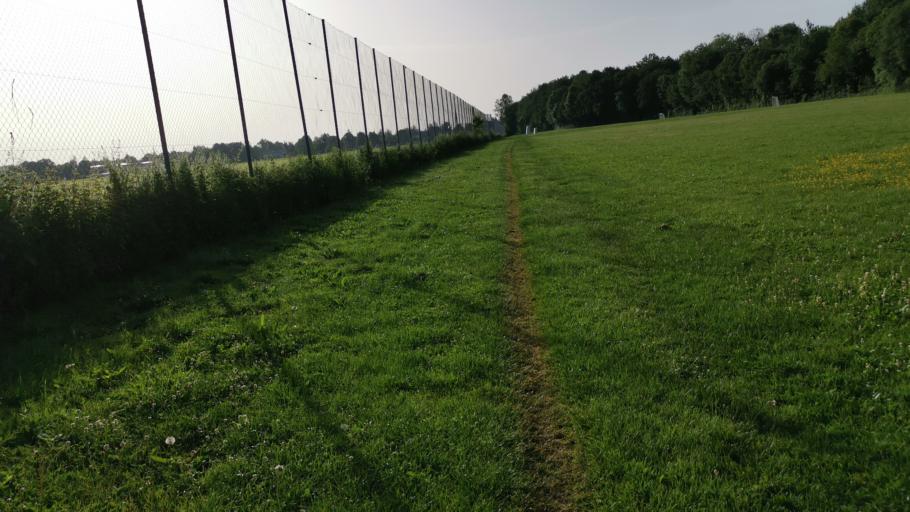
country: DE
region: Bavaria
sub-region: Upper Bavaria
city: Pullach im Isartal
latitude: 48.0630
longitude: 11.5053
